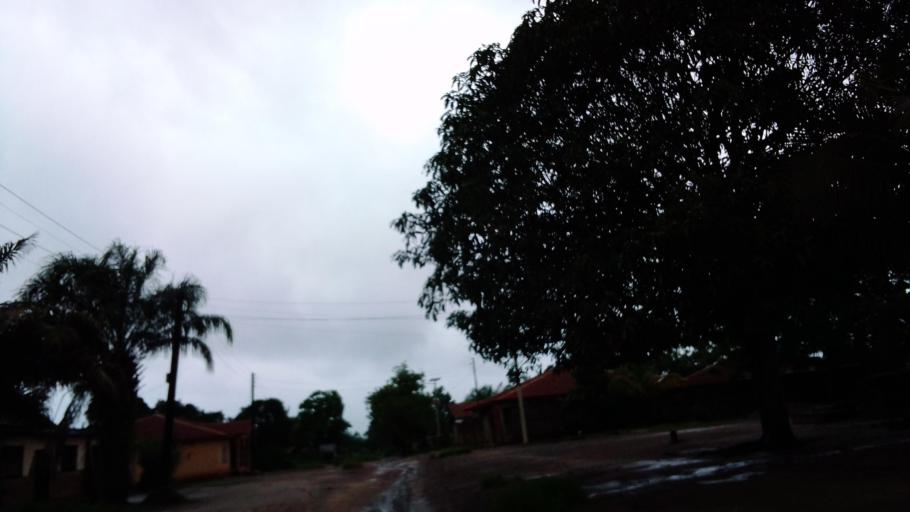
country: SL
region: Eastern Province
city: Kenema
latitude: 7.8483
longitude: -11.2048
